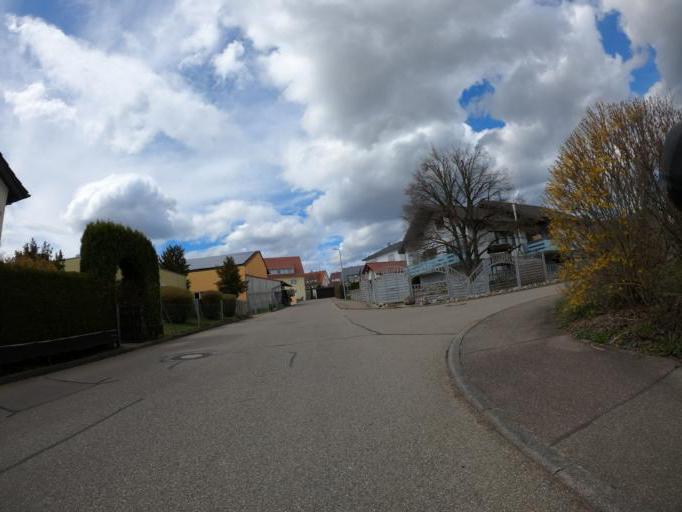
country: DE
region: Baden-Wuerttemberg
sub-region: Tuebingen Region
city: Pfullingen
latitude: 48.3912
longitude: 9.1835
